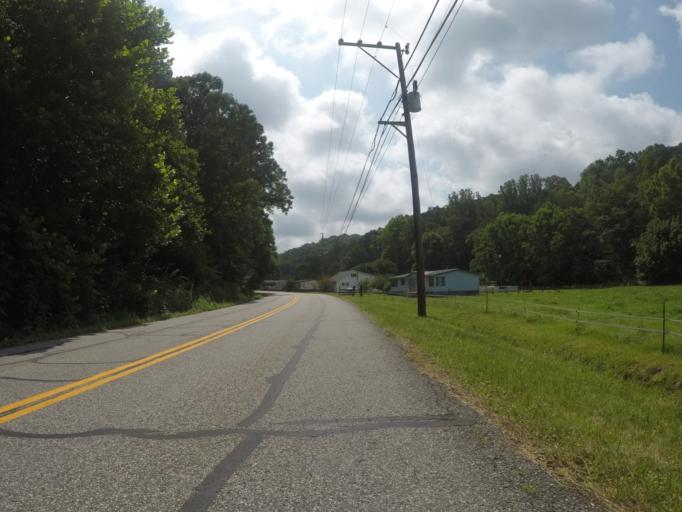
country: US
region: Kentucky
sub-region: Boyd County
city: Meads
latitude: 38.4134
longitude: -82.6807
